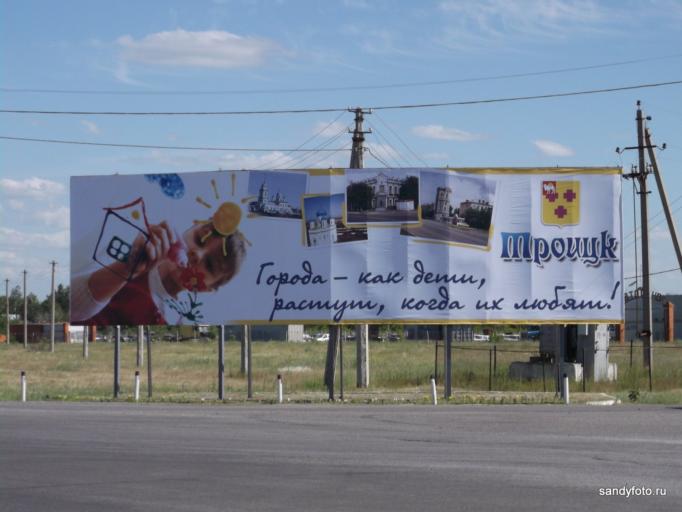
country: RU
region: Chelyabinsk
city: Troitsk
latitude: 54.0873
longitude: 61.4984
